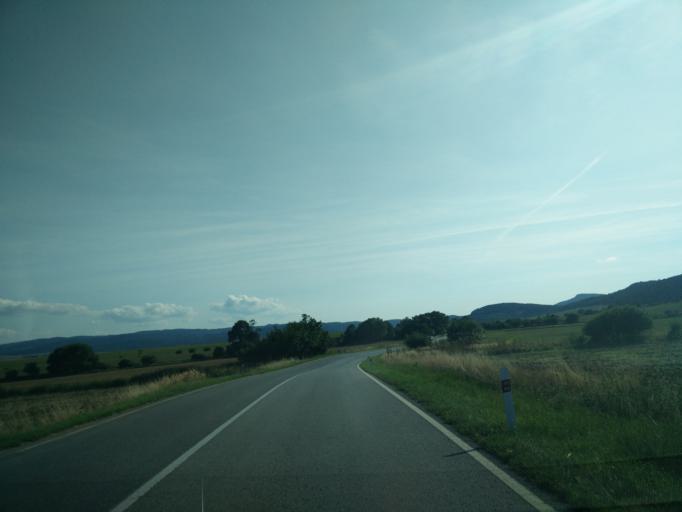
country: SK
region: Nitriansky
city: Handlova
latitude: 48.9202
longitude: 18.7755
